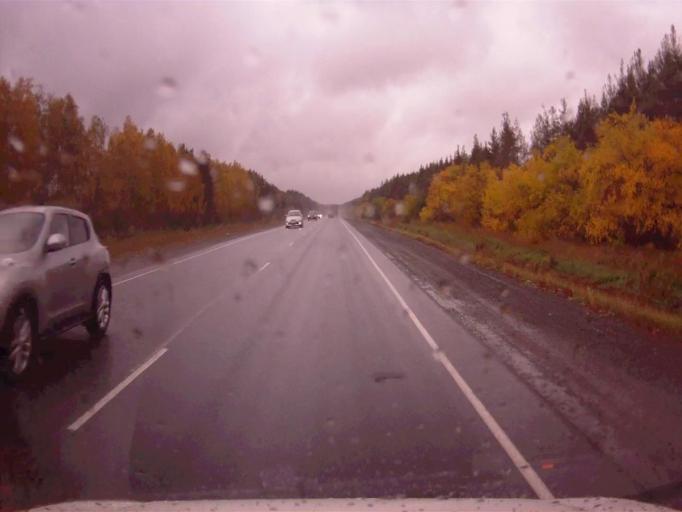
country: RU
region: Chelyabinsk
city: Roshchino
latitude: 55.3560
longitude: 61.2593
